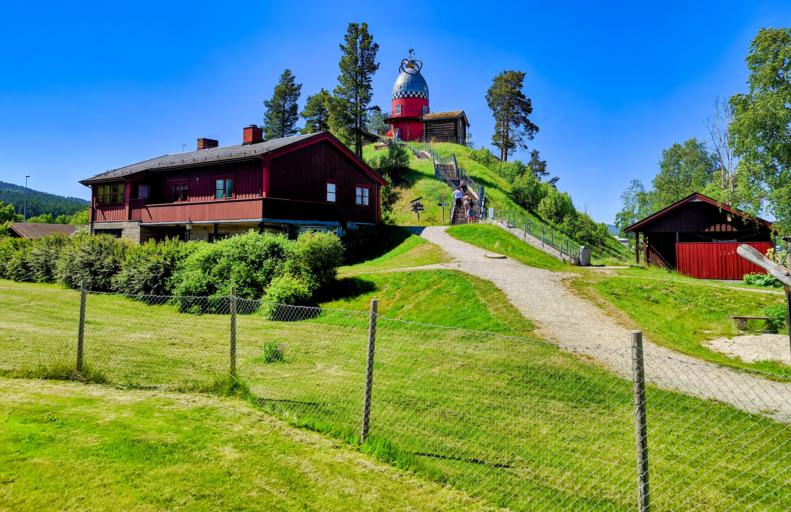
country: NO
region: Hedmark
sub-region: Alvdal
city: Alvdal
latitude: 62.1136
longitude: 10.6209
